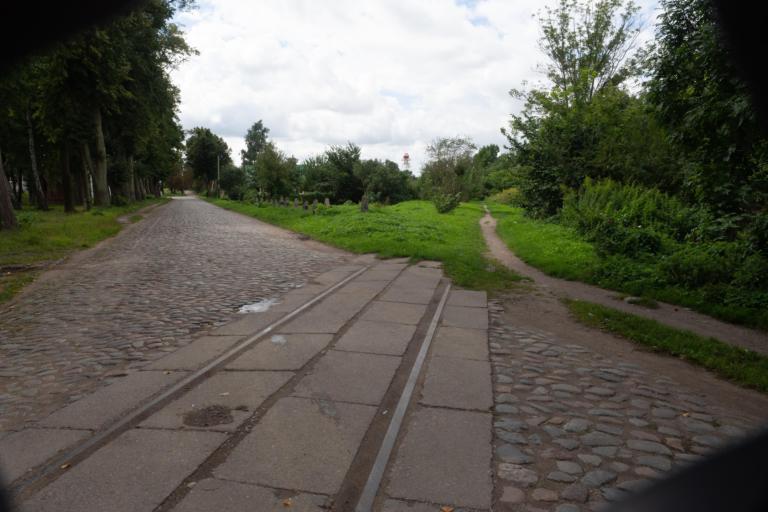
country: RU
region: Kaliningrad
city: Zheleznodorozhnyy
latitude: 54.3588
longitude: 21.3247
